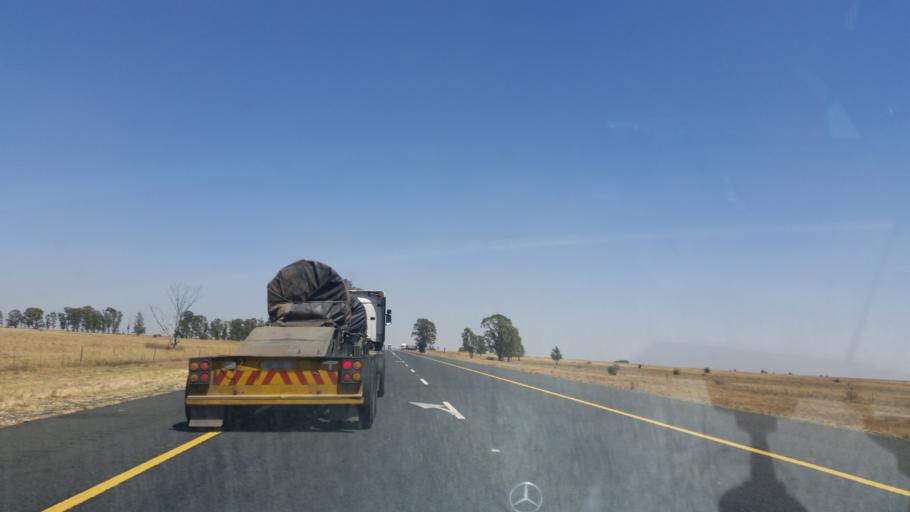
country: ZA
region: Orange Free State
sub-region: Lejweleputswa District Municipality
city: Winburg
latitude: -28.6392
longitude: 26.8924
